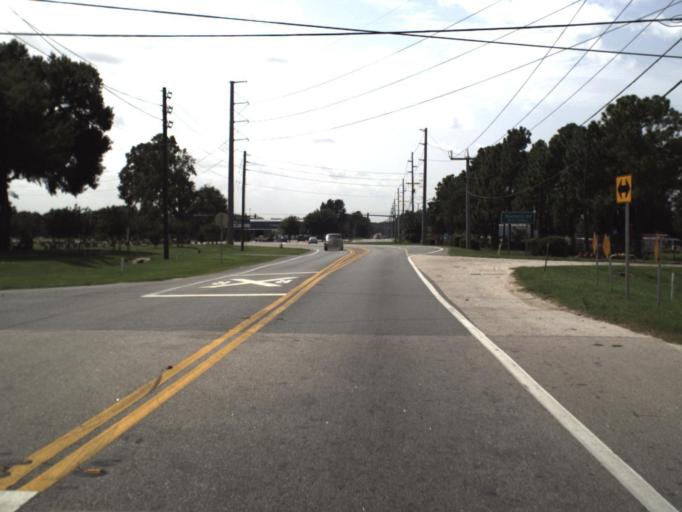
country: US
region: Florida
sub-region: Polk County
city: Auburndale
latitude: 28.0549
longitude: -81.8133
